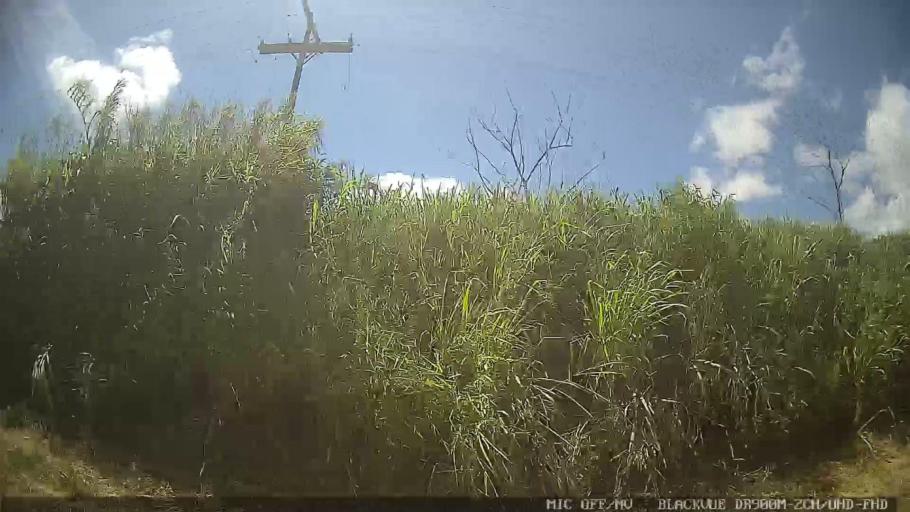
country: BR
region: Sao Paulo
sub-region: Amparo
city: Amparo
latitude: -22.8274
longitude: -46.7011
